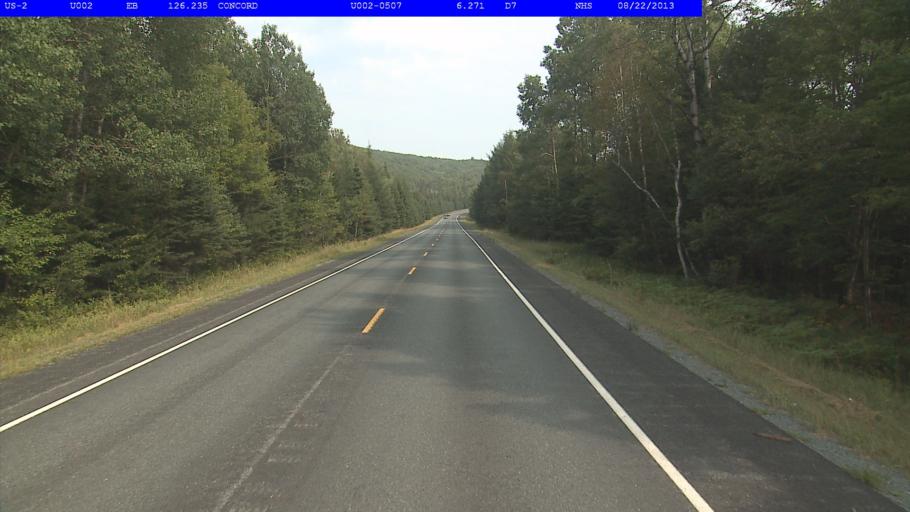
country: US
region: Vermont
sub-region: Caledonia County
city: Lyndonville
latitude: 44.4664
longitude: -71.8413
